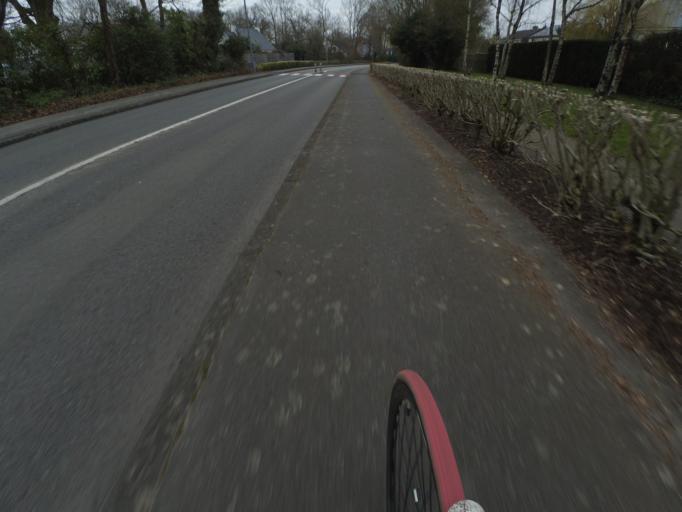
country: FR
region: Pays de la Loire
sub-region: Departement de la Loire-Atlantique
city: Sainte-Luce-sur-Loire
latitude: 47.2744
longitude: -1.4834
